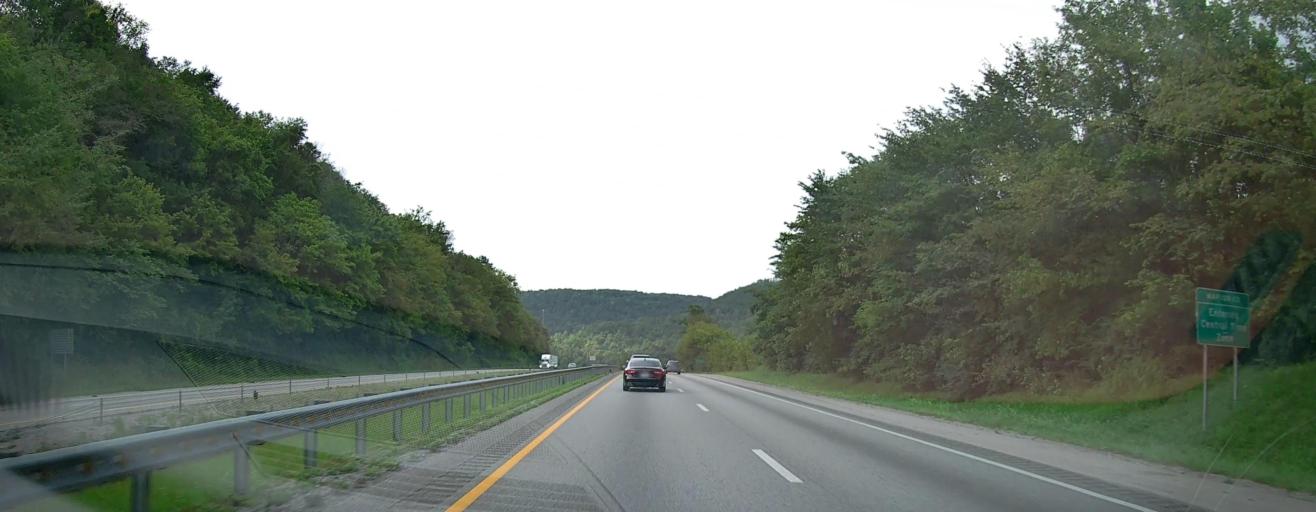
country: US
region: Georgia
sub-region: Walker County
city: Lookout Mountain
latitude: 34.9873
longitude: -85.4715
